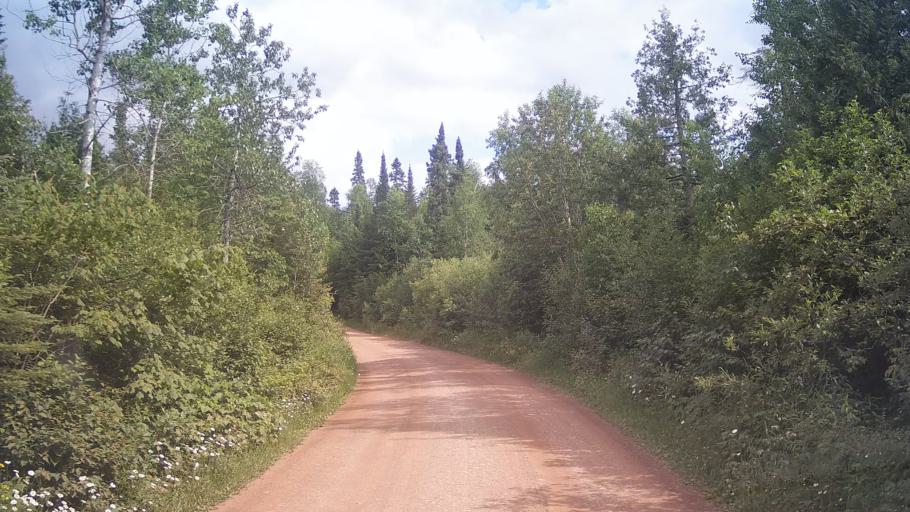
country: CA
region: Ontario
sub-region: Thunder Bay District
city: Thunder Bay
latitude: 48.6716
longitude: -88.6683
